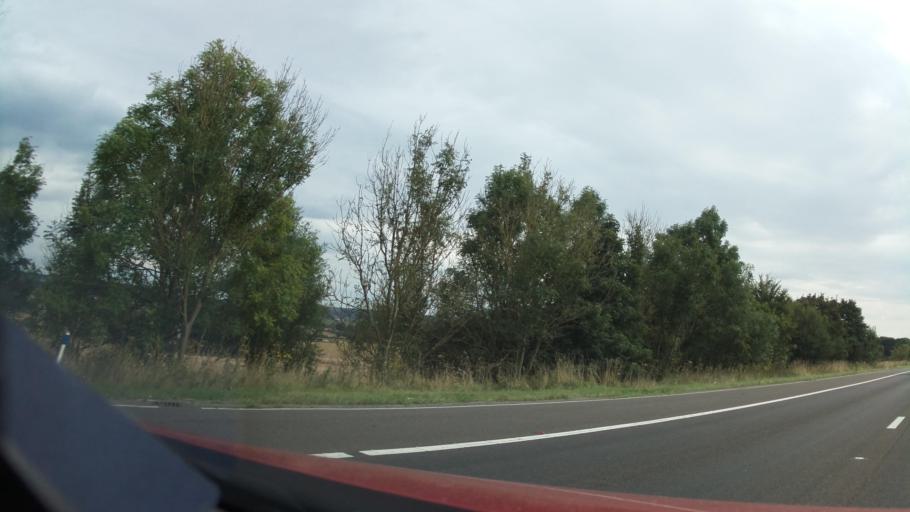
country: GB
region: England
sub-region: County Durham
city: Durham
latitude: 54.7790
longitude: -1.5329
